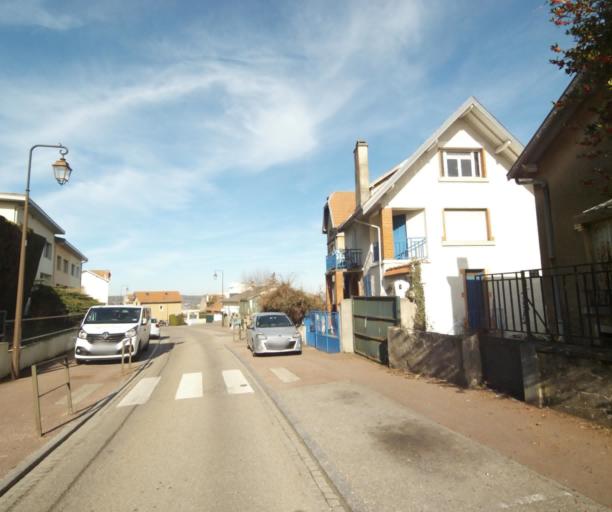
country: FR
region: Lorraine
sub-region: Departement de Meurthe-et-Moselle
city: Villers-les-Nancy
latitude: 48.6598
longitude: 6.1653
